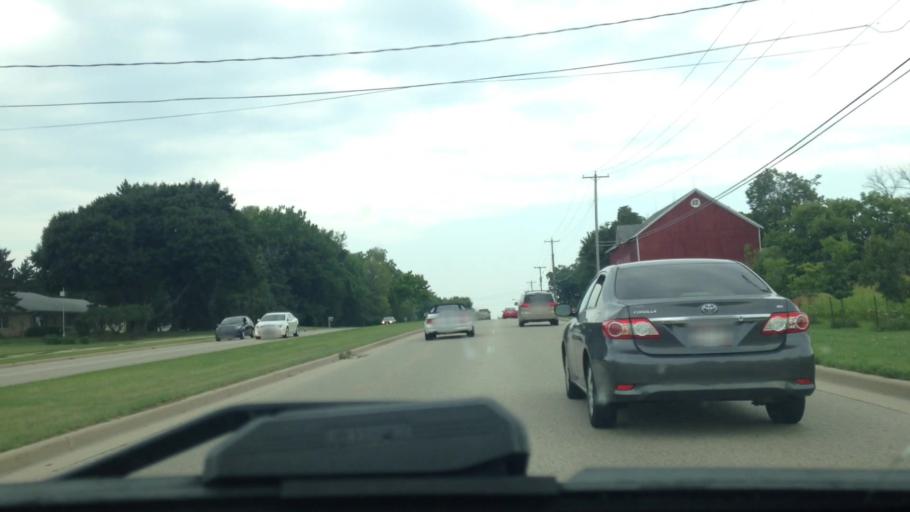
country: US
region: Wisconsin
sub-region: Waukesha County
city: Menomonee Falls
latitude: 43.1389
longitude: -88.1046
